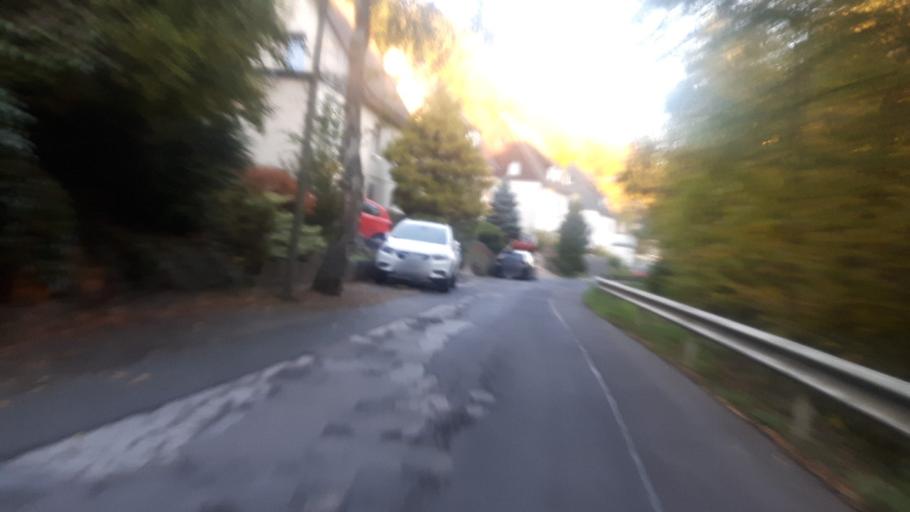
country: DE
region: Rheinland-Pfalz
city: Mudersbach
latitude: 50.8419
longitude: 7.9785
